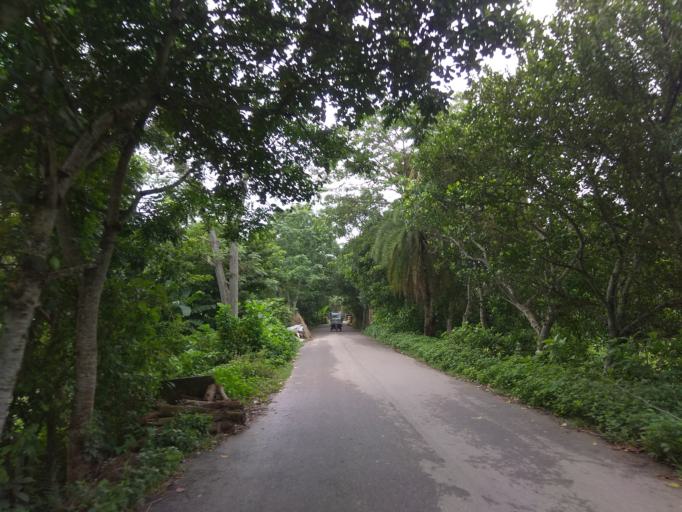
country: BD
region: Dhaka
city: Dohar
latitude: 23.4466
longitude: 90.0625
